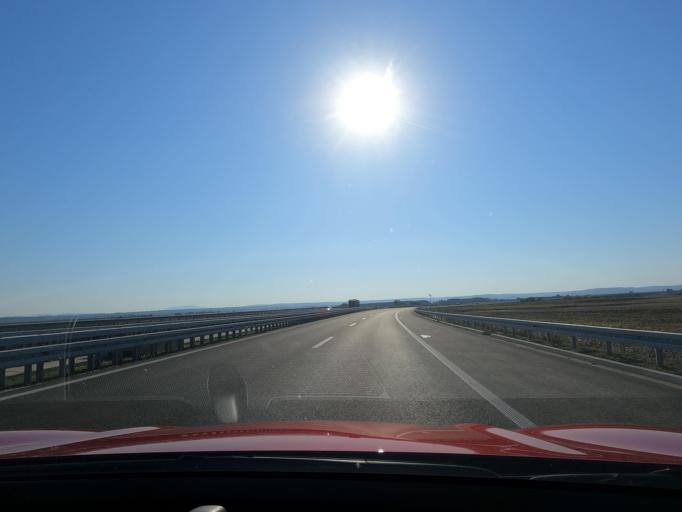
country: RS
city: Boljevci
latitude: 44.7255
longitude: 20.2532
